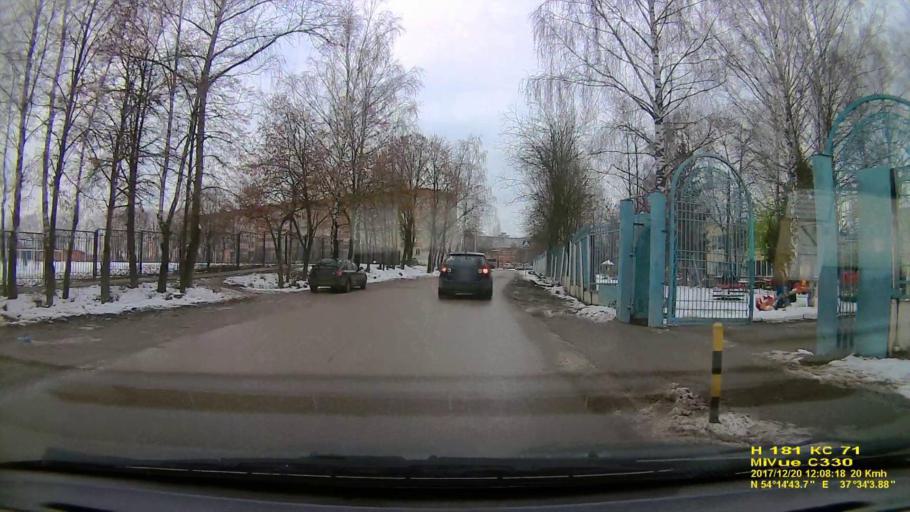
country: RU
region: Tula
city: Gorelki
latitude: 54.2455
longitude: 37.5676
